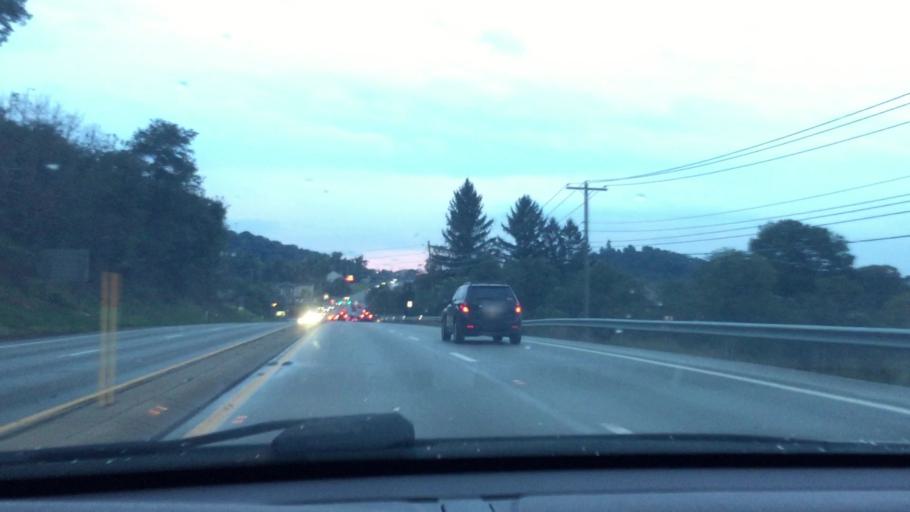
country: US
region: Pennsylvania
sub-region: Washington County
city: McGovern
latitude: 40.2085
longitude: -80.1989
